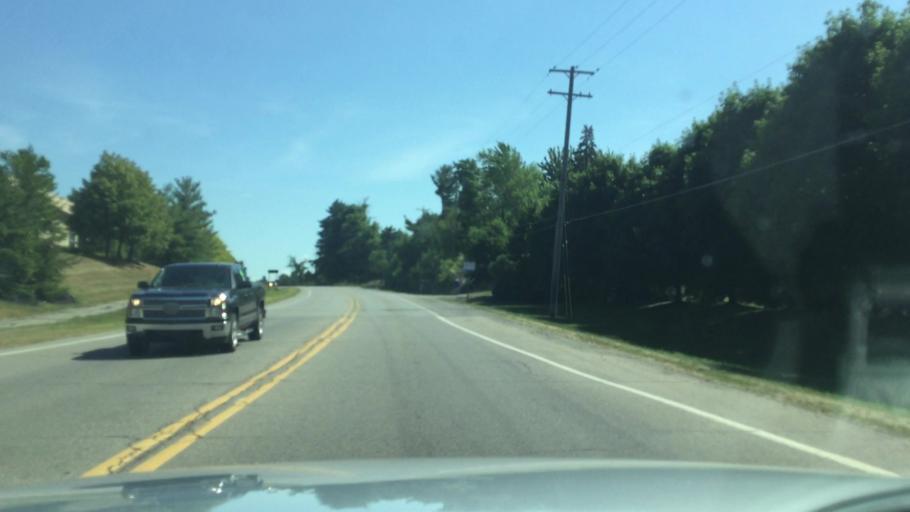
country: US
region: Michigan
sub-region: Genesee County
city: Grand Blanc
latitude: 42.9171
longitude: -83.6464
